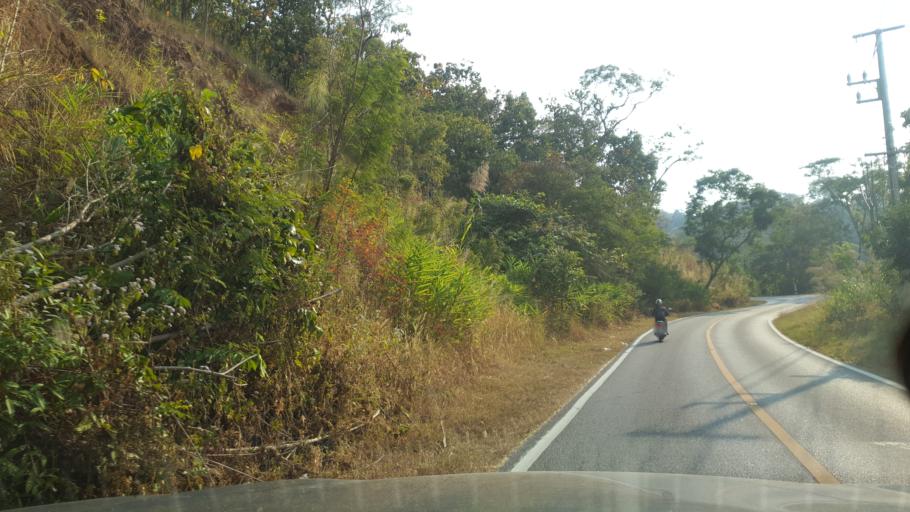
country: TH
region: Chiang Mai
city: Mae On
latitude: 18.7236
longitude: 99.2680
